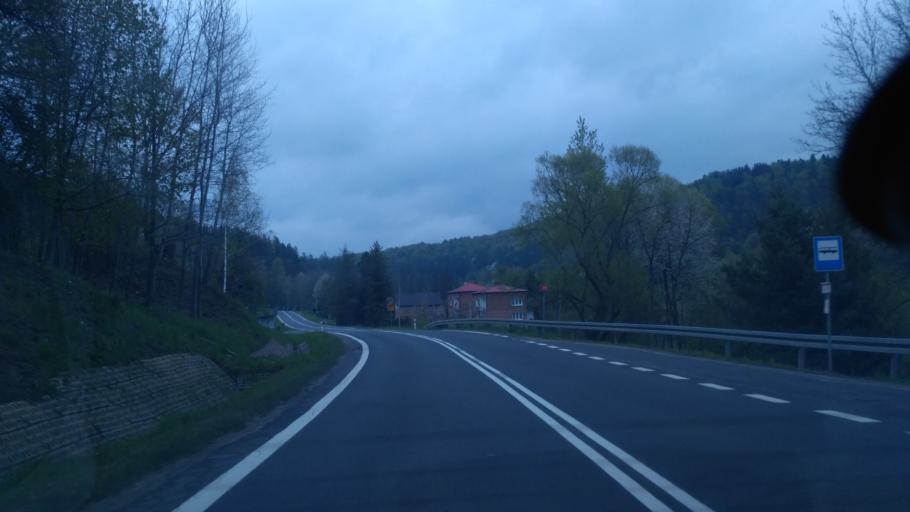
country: PL
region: Subcarpathian Voivodeship
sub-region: Powiat sanocki
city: Zagorz
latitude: 49.5321
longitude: 22.2969
